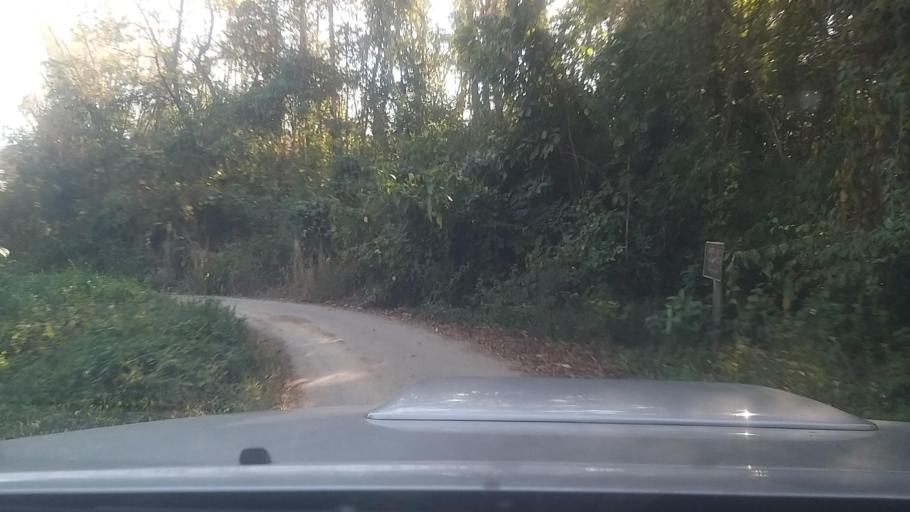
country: TH
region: Phrae
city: Phrae
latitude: 18.2709
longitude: 99.9872
